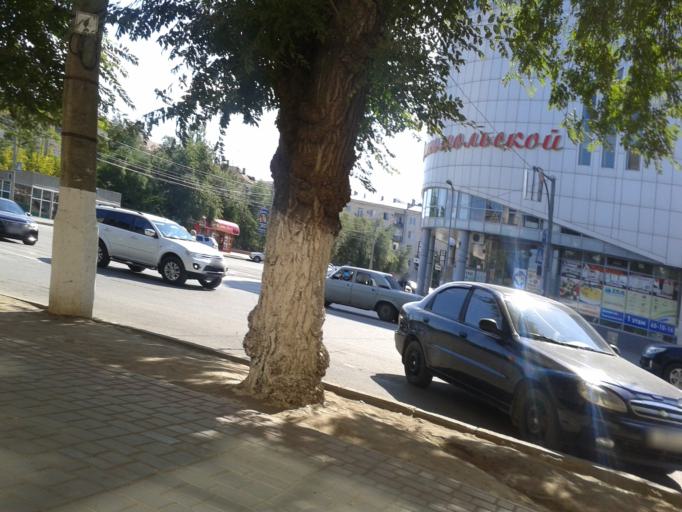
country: RU
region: Volgograd
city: Volgograd
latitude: 48.7078
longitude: 44.5226
